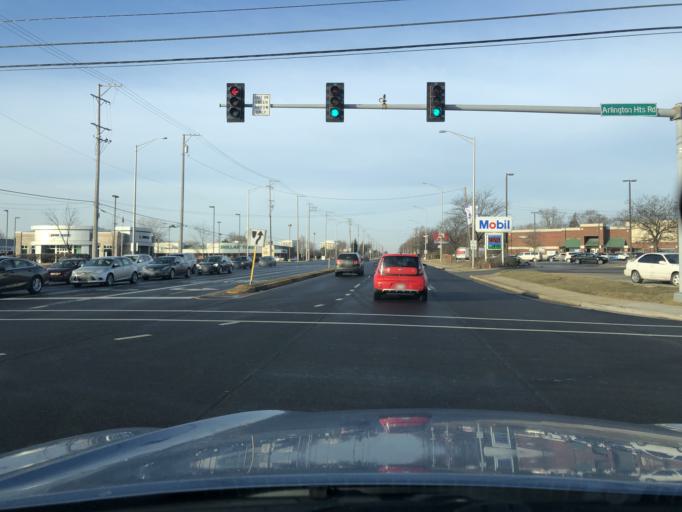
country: US
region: Illinois
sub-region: Cook County
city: Arlington Heights
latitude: 42.0515
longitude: -87.9824
